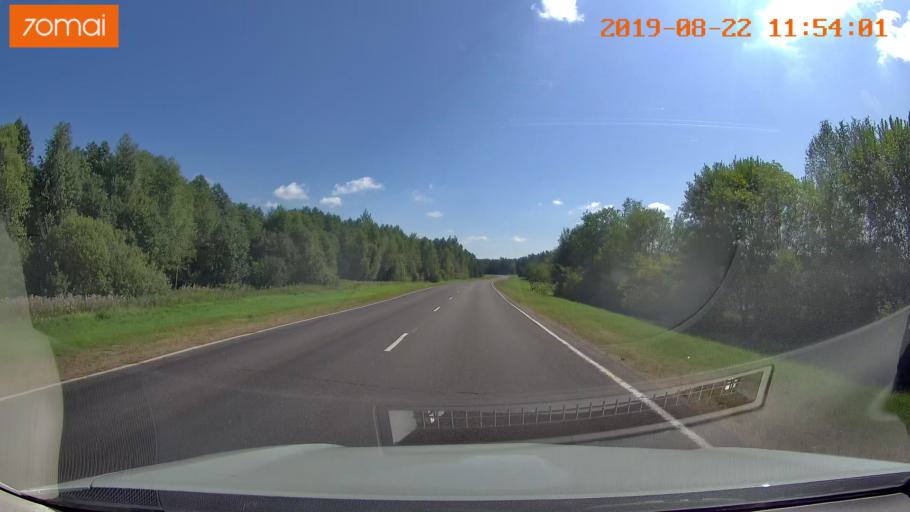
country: BY
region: Minsk
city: Uzda
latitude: 53.4358
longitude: 27.5149
